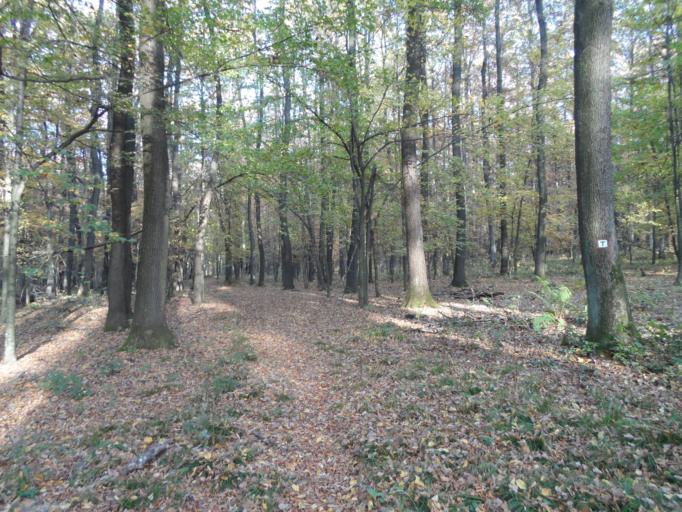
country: HU
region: Veszprem
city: Urkut
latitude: 47.1940
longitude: 17.6561
